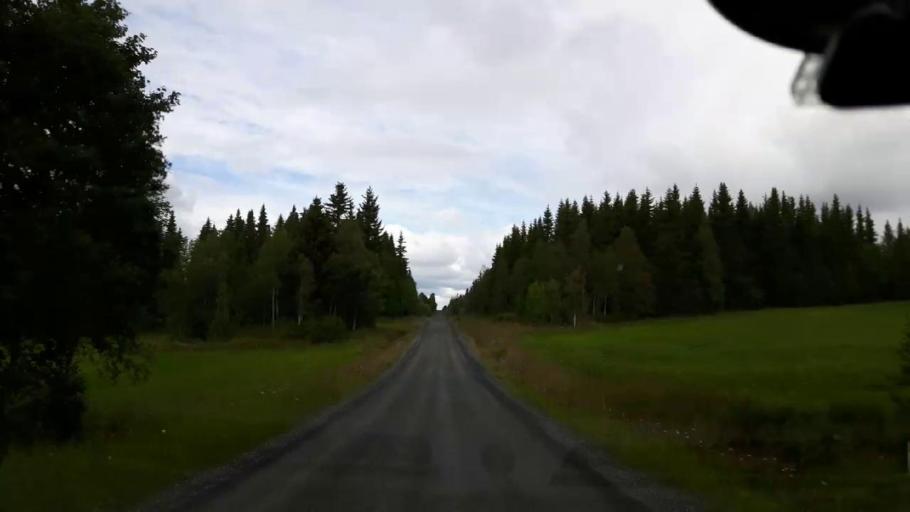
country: SE
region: Jaemtland
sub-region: Krokoms Kommun
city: Valla
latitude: 63.5041
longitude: 13.9594
